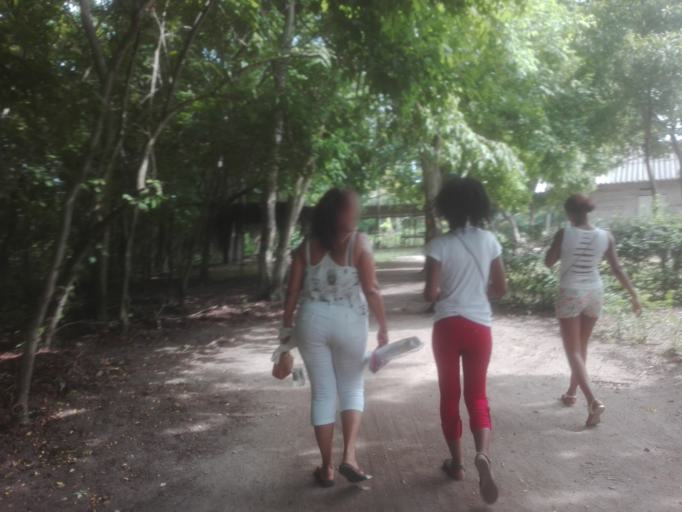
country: CO
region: Bolivar
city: Turbana
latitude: 10.1778
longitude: -75.7403
